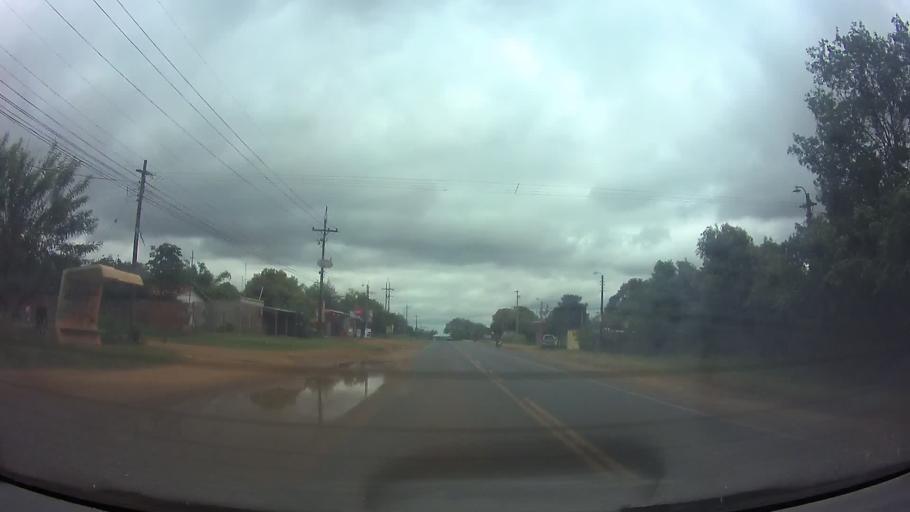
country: PY
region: Central
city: Guarambare
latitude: -25.5016
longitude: -57.4965
